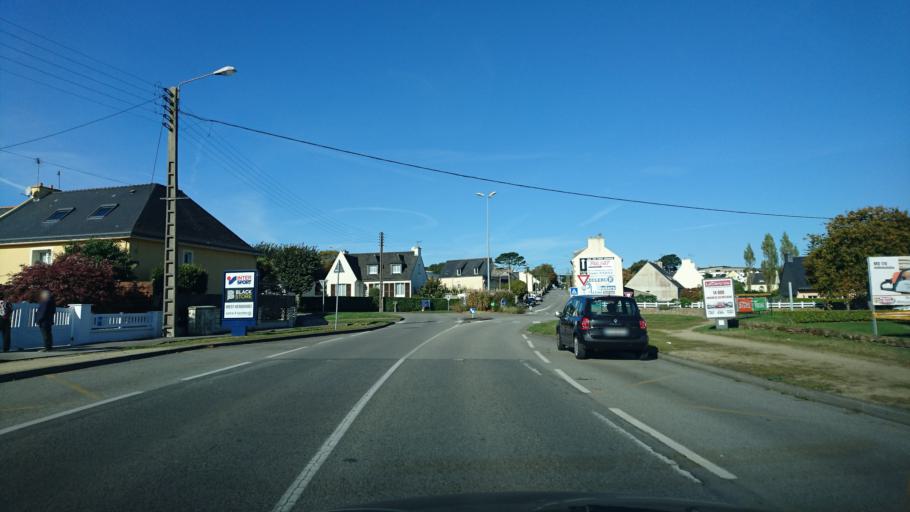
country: FR
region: Brittany
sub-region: Departement du Finistere
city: Saint-Renan
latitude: 48.4262
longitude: -4.6146
